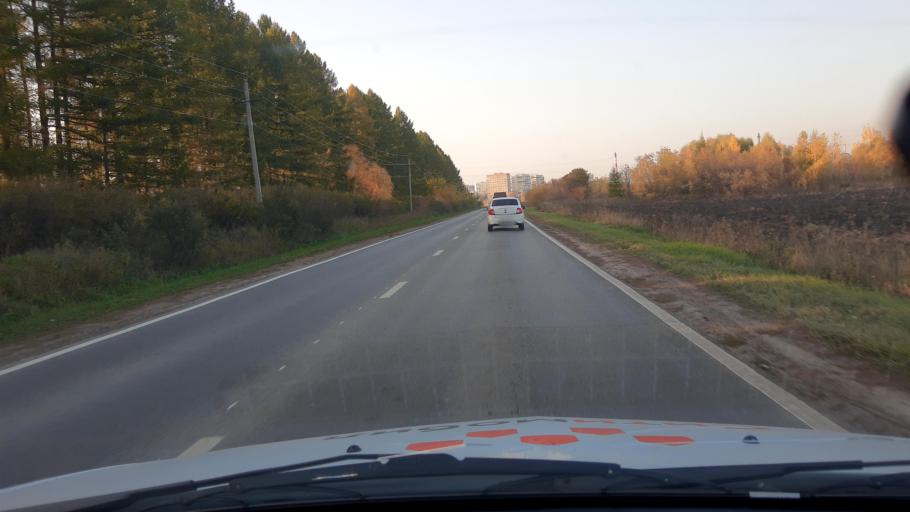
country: RU
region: Bashkortostan
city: Iglino
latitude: 54.7470
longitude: 56.2526
